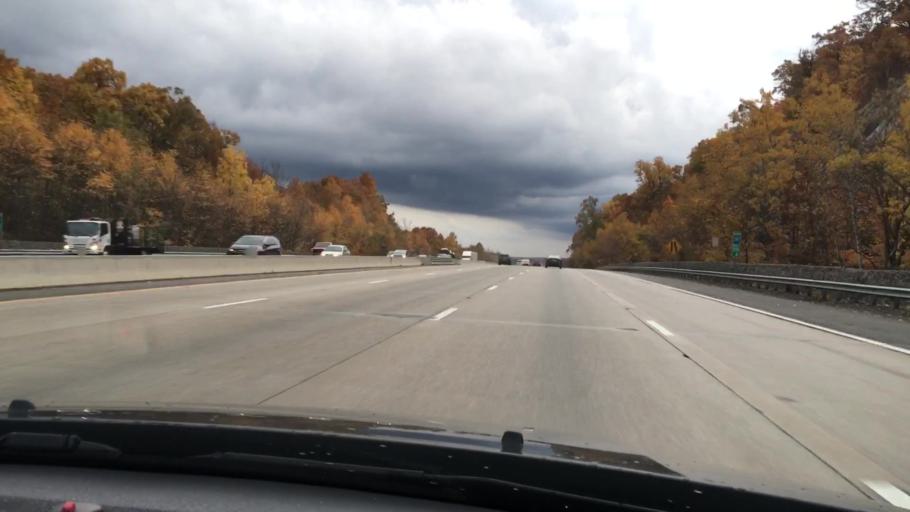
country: US
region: New Jersey
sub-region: Passaic County
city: Bloomingdale
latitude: 40.9565
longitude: -74.3389
